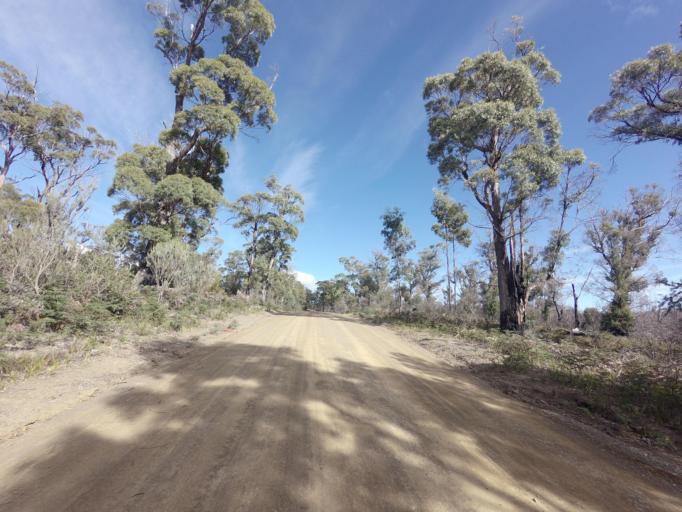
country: AU
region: Tasmania
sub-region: Clarence
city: Sandford
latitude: -42.9781
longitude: 147.7167
